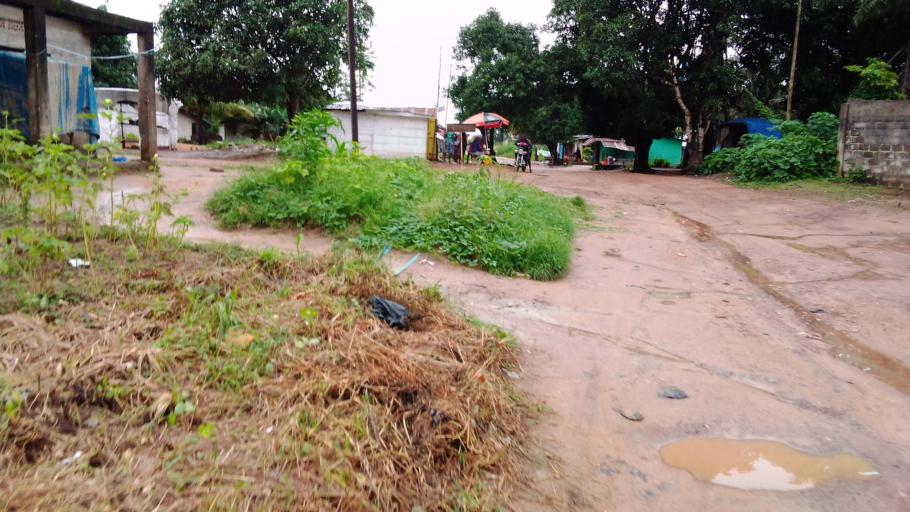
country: SL
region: Eastern Province
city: Kenema
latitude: 7.8992
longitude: -11.1856
